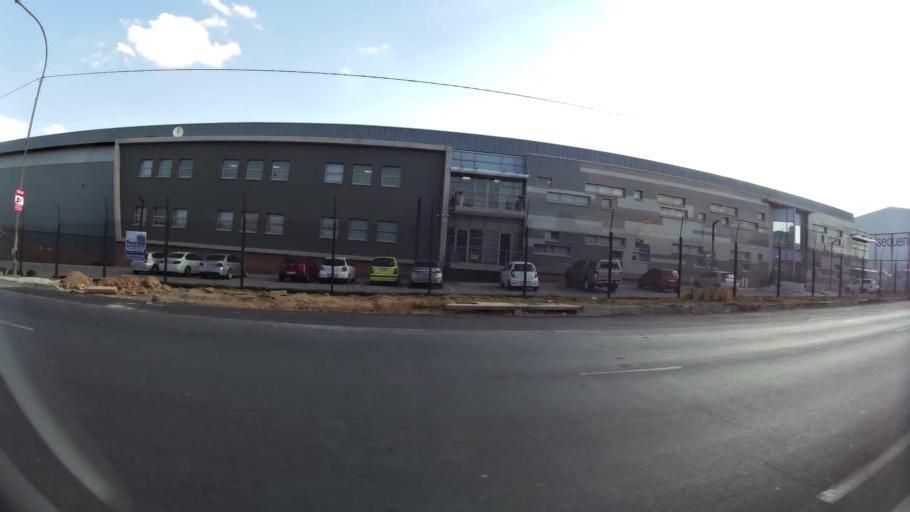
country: ZA
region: Gauteng
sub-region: City of Johannesburg Metropolitan Municipality
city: Johannesburg
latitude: -26.2583
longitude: 27.9731
